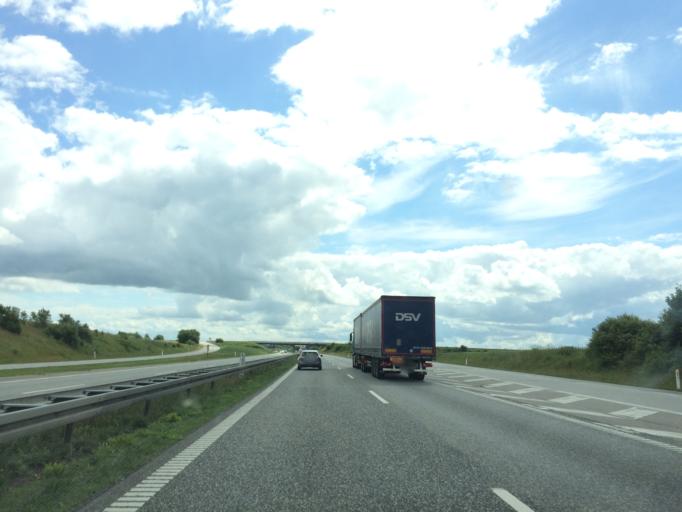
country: DK
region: North Denmark
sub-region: Mariagerfjord Kommune
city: Hobro
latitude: 56.6713
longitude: 9.7332
